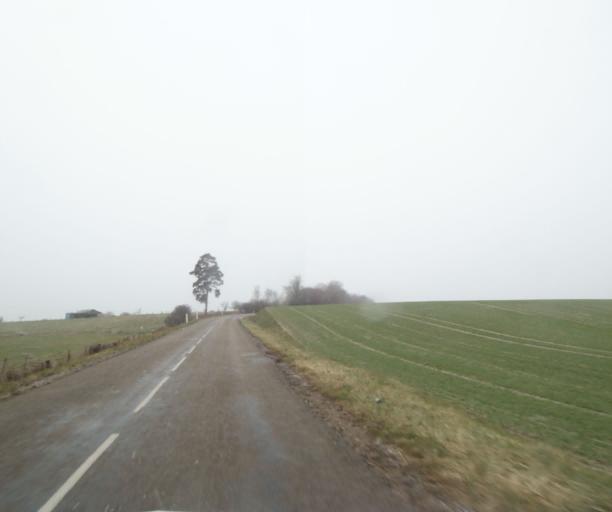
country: FR
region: Champagne-Ardenne
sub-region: Departement de la Haute-Marne
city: Wassy
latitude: 48.5145
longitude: 5.0128
